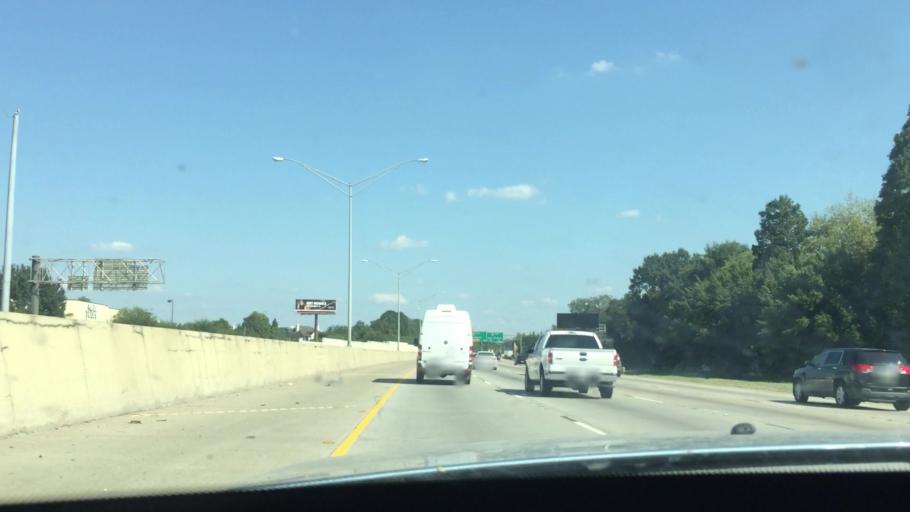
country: US
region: Louisiana
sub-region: East Baton Rouge Parish
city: Baton Rouge
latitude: 30.4218
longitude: -91.1286
